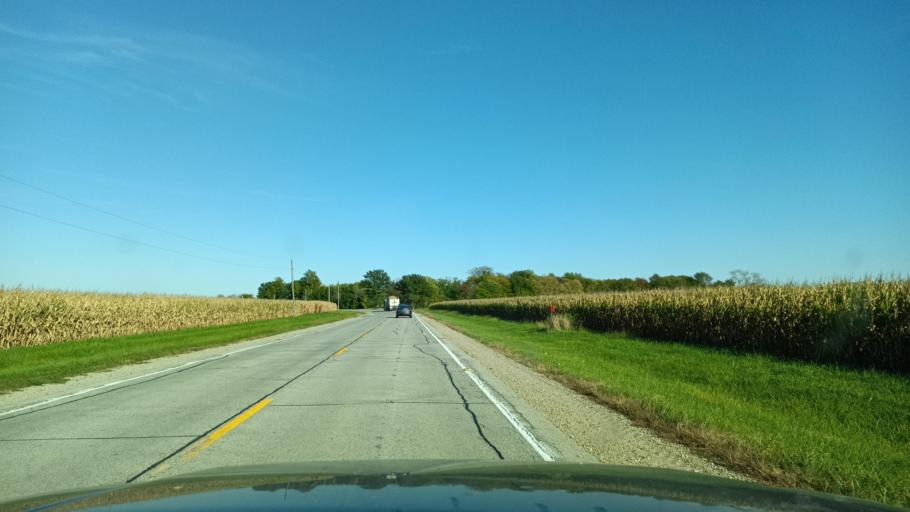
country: US
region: Illinois
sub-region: De Witt County
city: Farmer City
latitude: 40.2238
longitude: -88.6990
